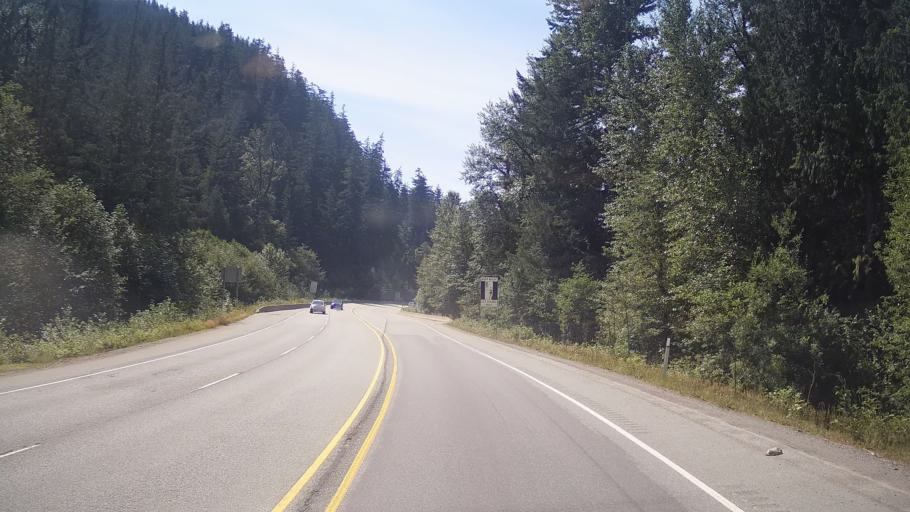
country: CA
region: British Columbia
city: Whistler
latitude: 49.9464
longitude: -123.1667
